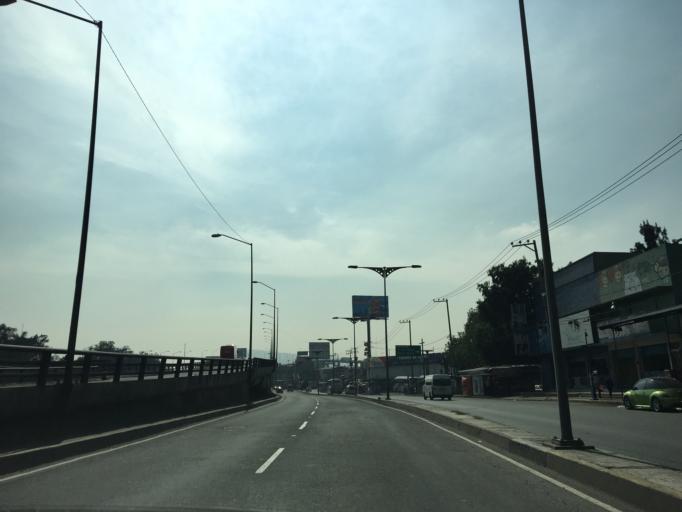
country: MX
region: Mexico
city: Los Reyes La Paz
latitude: 19.3626
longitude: -99.0034
